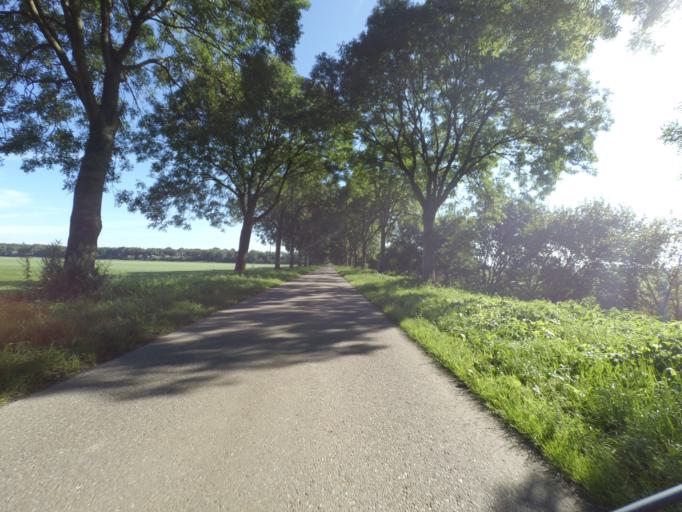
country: NL
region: Flevoland
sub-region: Gemeente Zeewolde
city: Zeewolde
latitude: 52.3905
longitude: 5.4944
